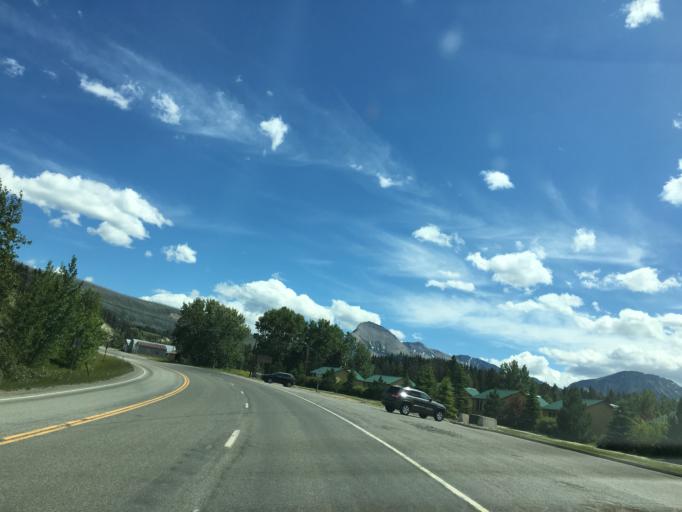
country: US
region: Montana
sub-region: Glacier County
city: North Browning
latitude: 48.7417
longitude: -113.4292
